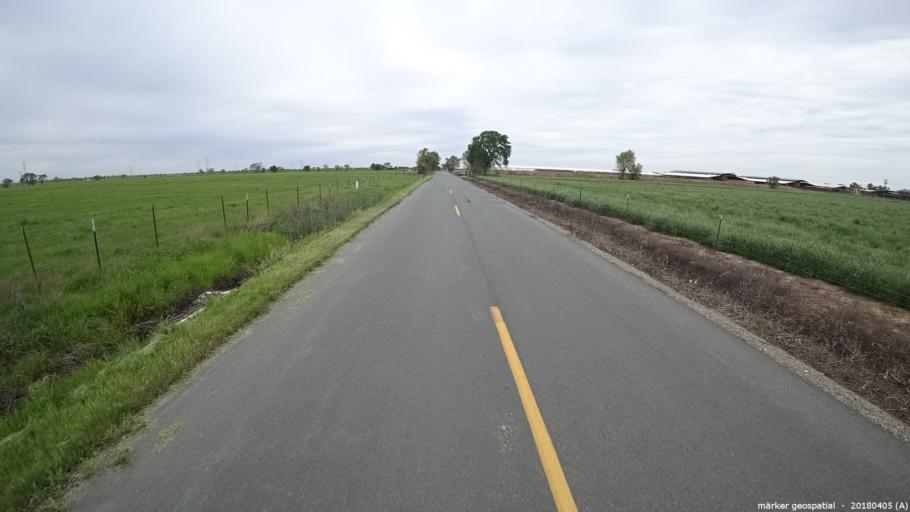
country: US
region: California
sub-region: Sacramento County
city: Galt
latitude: 38.2498
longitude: -121.3554
